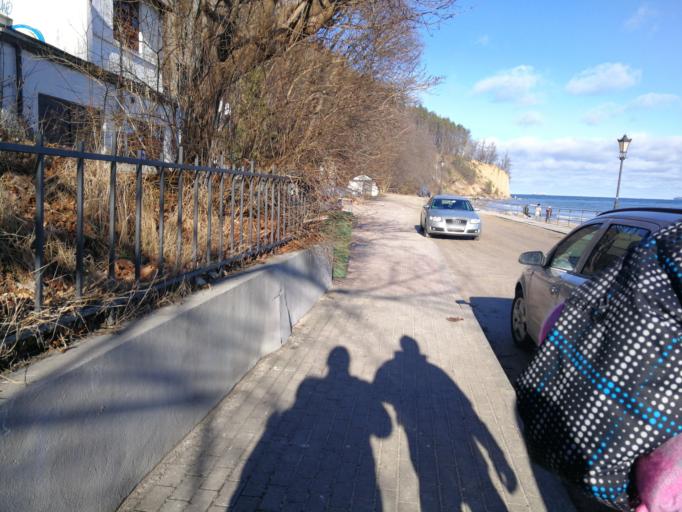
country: PL
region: Pomeranian Voivodeship
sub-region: Sopot
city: Sopot
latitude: 54.4819
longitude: 18.5649
